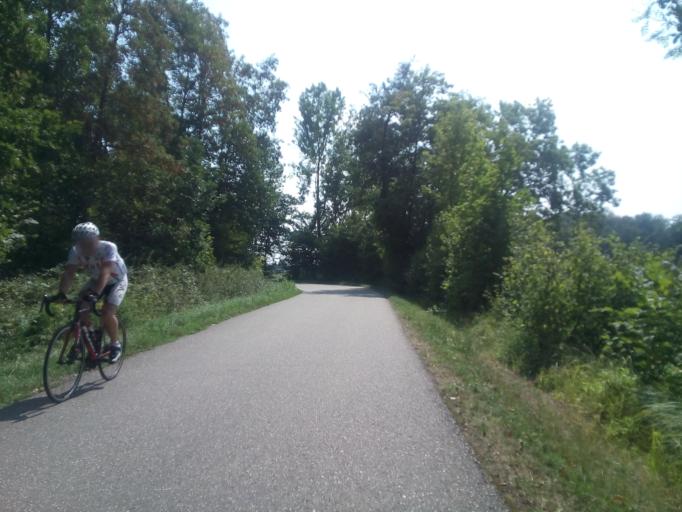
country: DE
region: Baden-Wuerttemberg
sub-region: Freiburg Region
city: Willstatt
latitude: 48.5886
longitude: 7.8954
